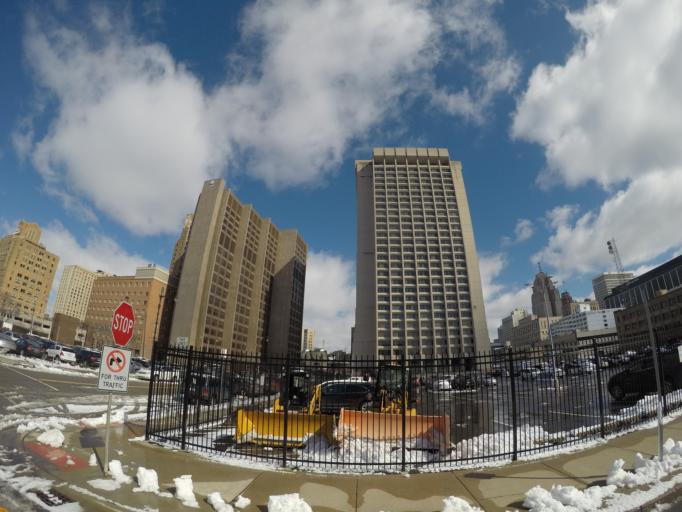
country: US
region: Michigan
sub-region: Wayne County
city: Detroit
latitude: 42.3306
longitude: -83.0550
